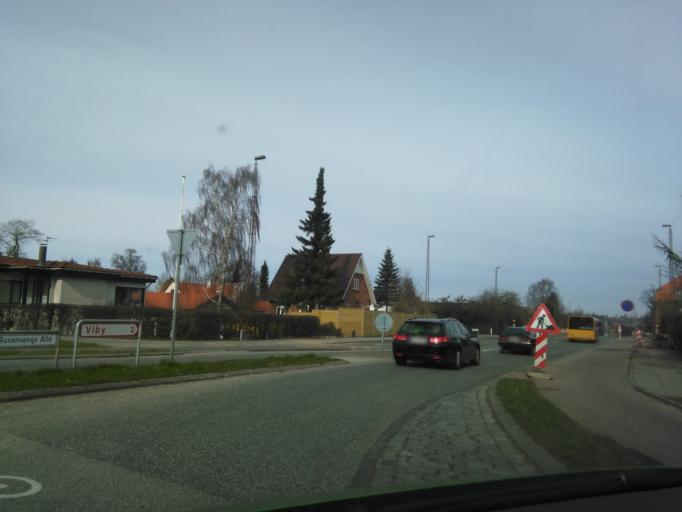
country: DK
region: Central Jutland
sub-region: Arhus Kommune
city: Arhus
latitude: 56.1269
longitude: 10.1842
